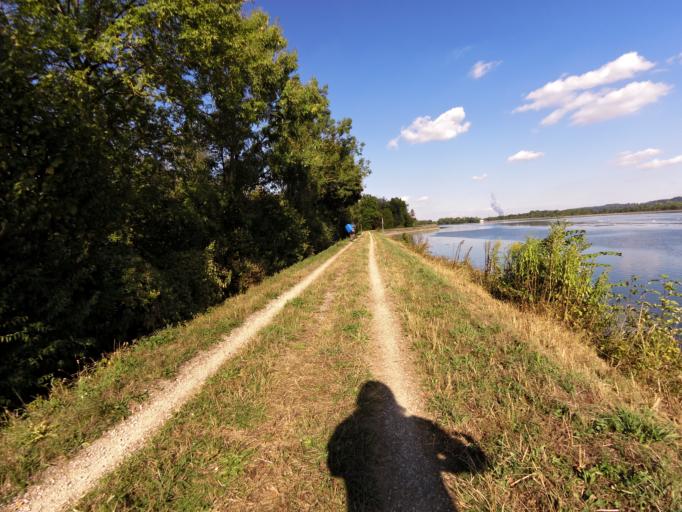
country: DE
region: Bavaria
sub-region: Lower Bavaria
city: Ergolding
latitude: 48.5757
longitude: 12.2017
